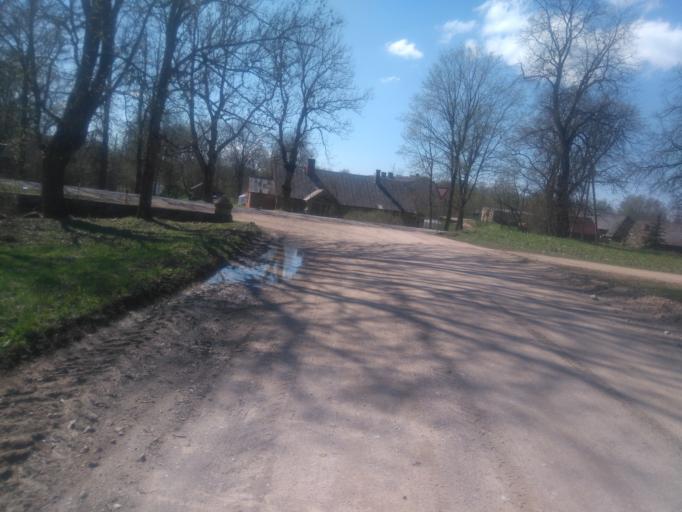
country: LV
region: Vecpiebalga
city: Vecpiebalga
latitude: 57.0216
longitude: 25.8310
